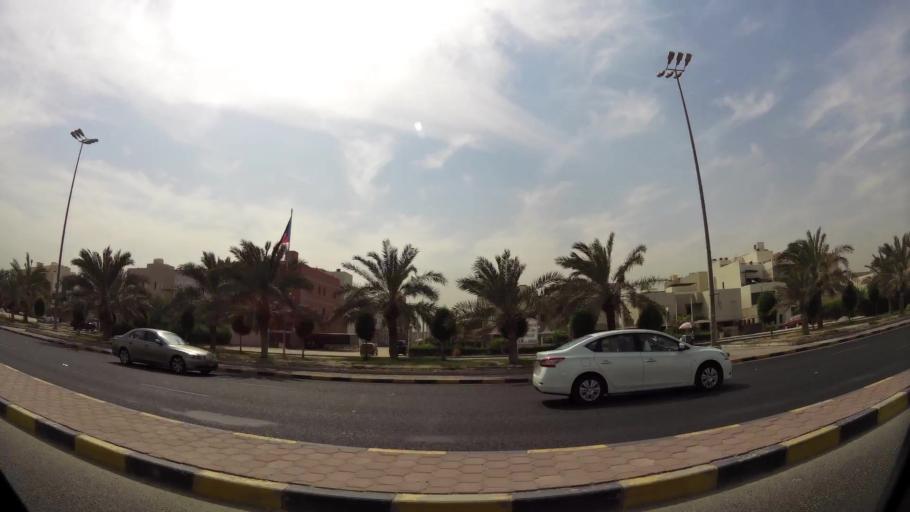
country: KW
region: Al Farwaniyah
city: Janub as Surrah
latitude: 29.2843
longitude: 48.0062
